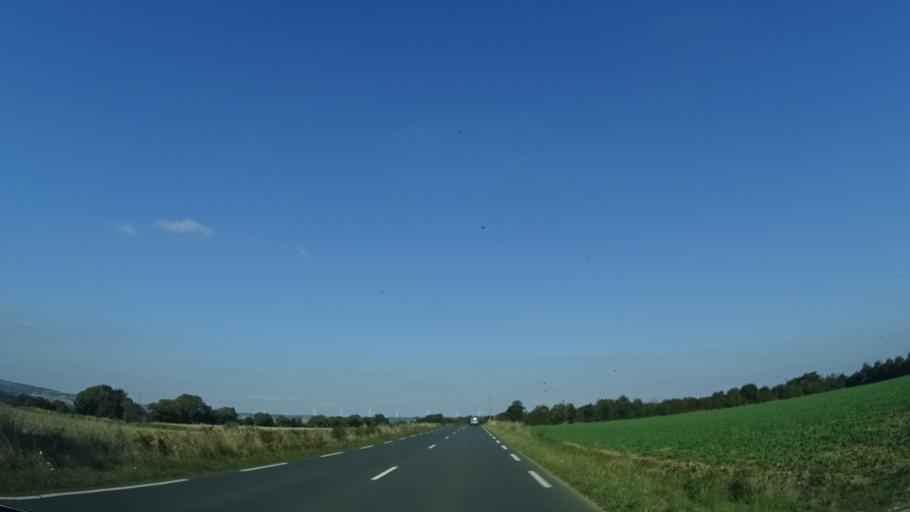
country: FR
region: Brittany
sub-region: Departement du Finistere
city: Plonevez-Porzay
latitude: 48.1355
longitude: -4.1856
